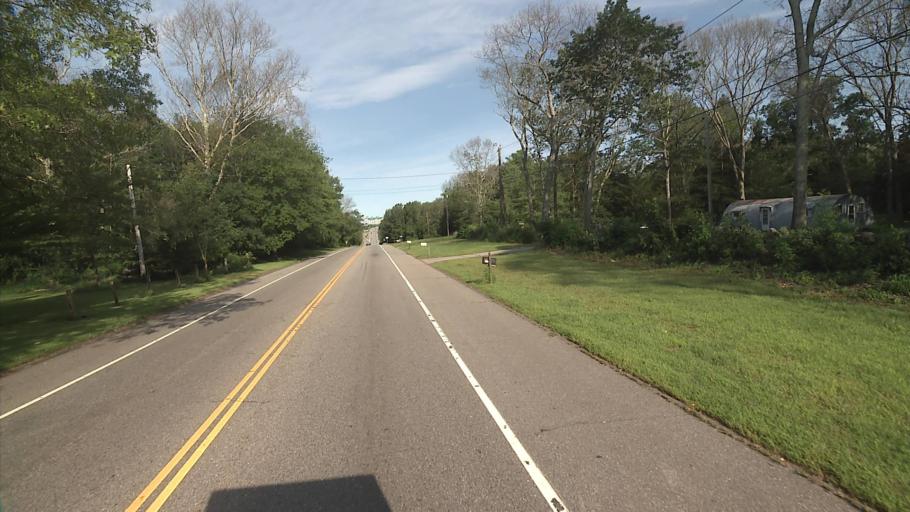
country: US
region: Connecticut
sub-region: New London County
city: Preston City
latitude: 41.4669
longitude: -71.9376
